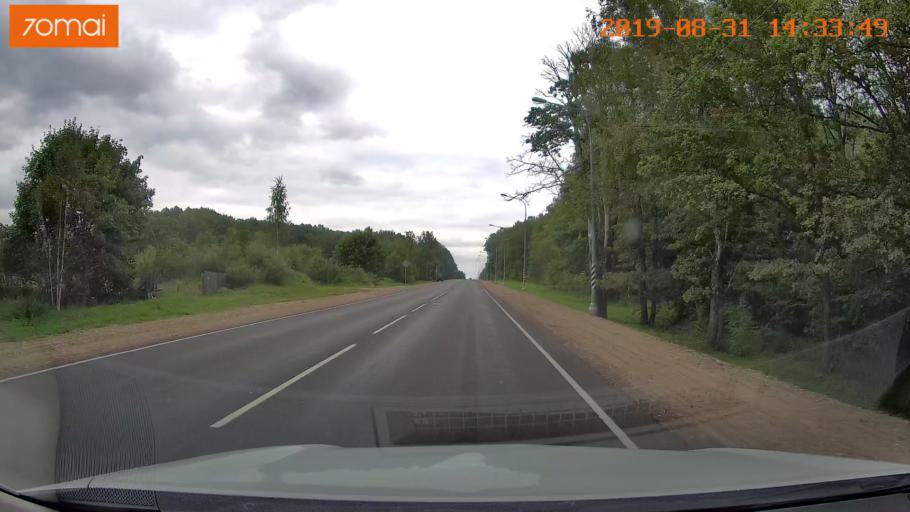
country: RU
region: Smolensk
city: Yekimovichi
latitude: 54.1541
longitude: 33.4266
